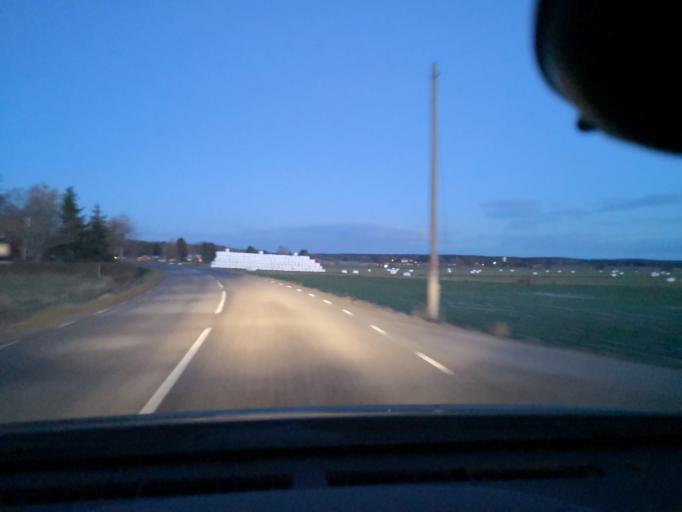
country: SE
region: Vaestmanland
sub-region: Sala Kommun
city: Sala
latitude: 59.8709
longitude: 16.7105
